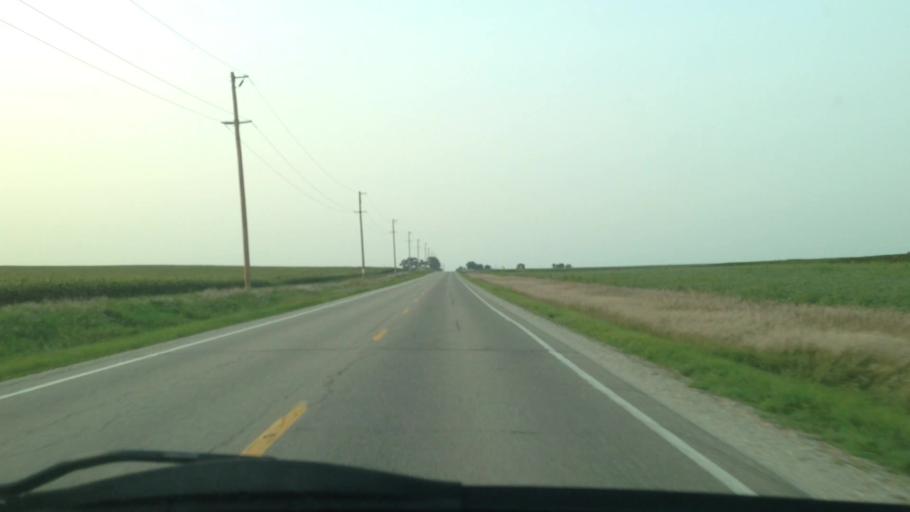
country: US
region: Iowa
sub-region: Iowa County
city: Marengo
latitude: 41.9533
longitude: -92.0852
